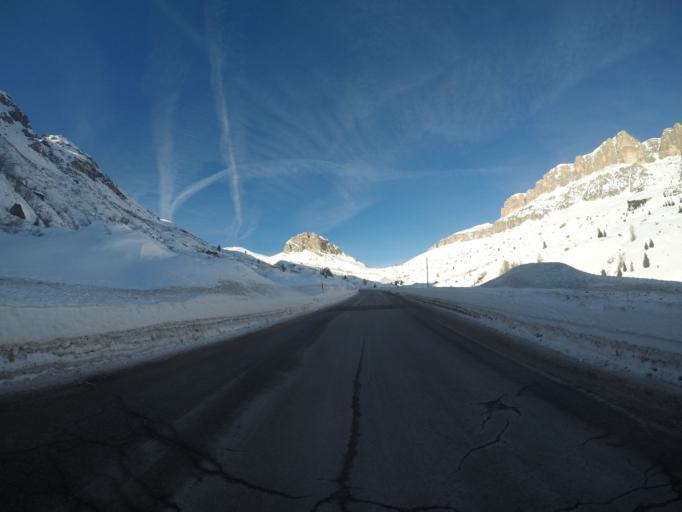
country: IT
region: Trentino-Alto Adige
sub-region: Provincia di Trento
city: Canazei
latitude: 46.4841
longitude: 11.8384
